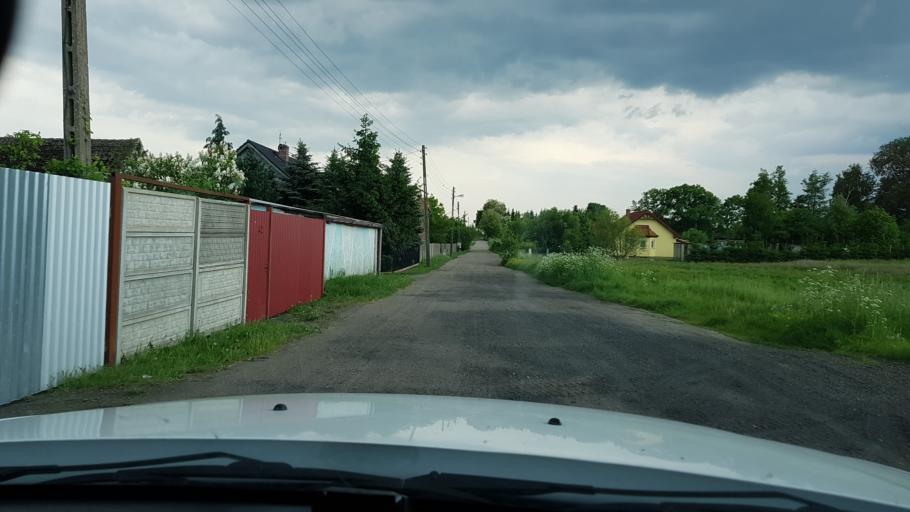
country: PL
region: West Pomeranian Voivodeship
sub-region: Powiat stargardzki
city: Stara Dabrowa
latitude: 53.3704
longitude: 15.1796
